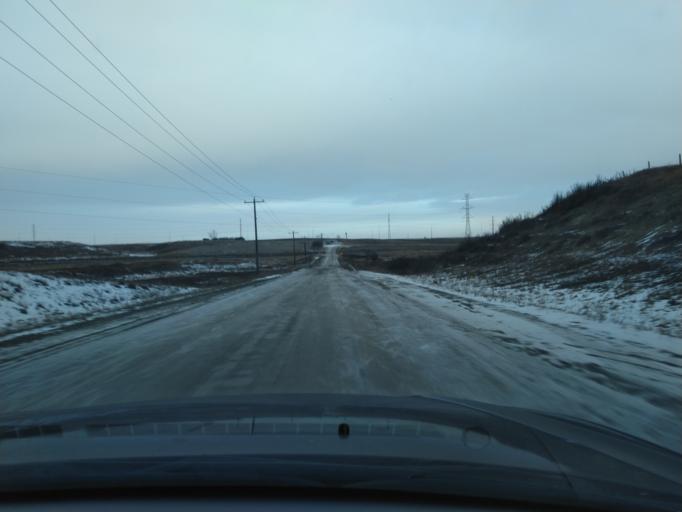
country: CA
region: Alberta
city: Airdrie
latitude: 51.1697
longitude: -114.0249
